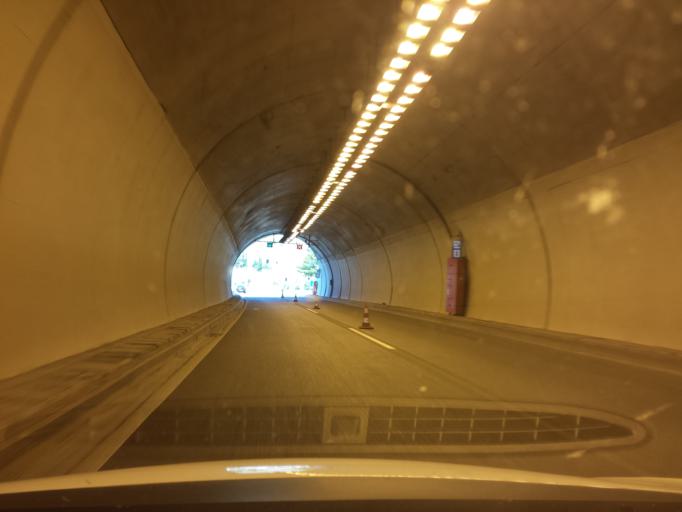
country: GR
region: West Greece
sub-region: Nomos Achaias
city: Rio
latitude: 38.2693
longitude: 21.7811
